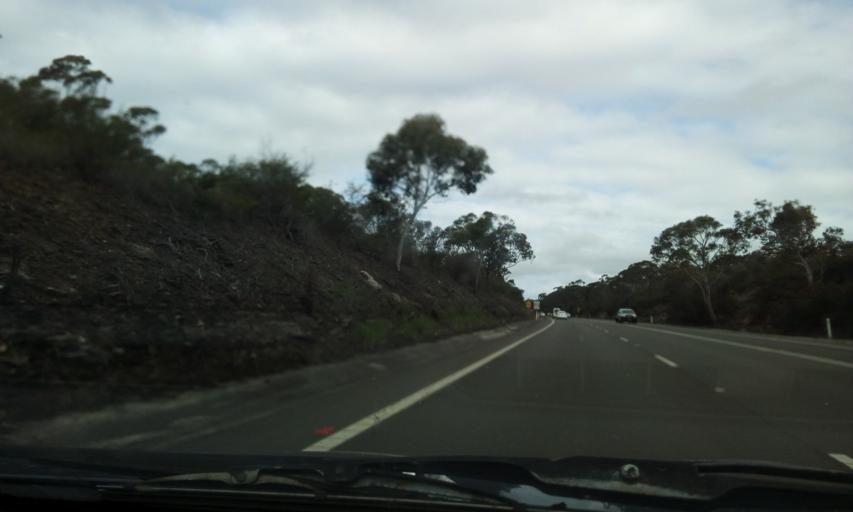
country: AU
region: New South Wales
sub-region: Wollondilly
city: Douglas Park
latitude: -34.2369
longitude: 150.8282
